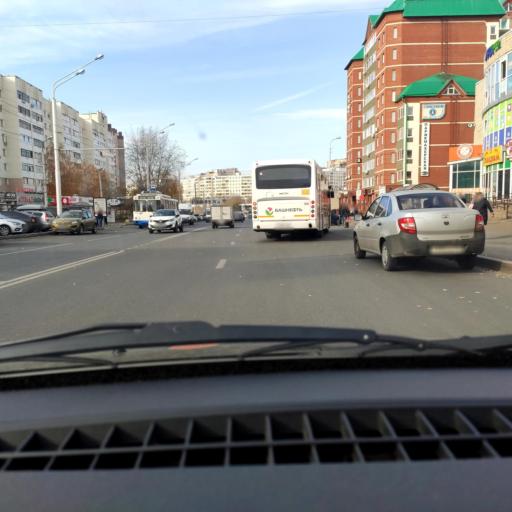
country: RU
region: Bashkortostan
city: Ufa
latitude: 54.6956
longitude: 55.9977
